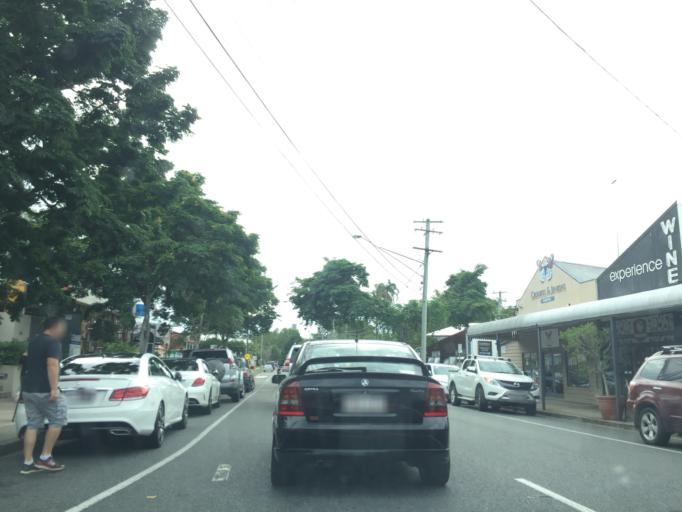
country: AU
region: Queensland
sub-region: Brisbane
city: Milton
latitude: -27.4662
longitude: 152.9973
